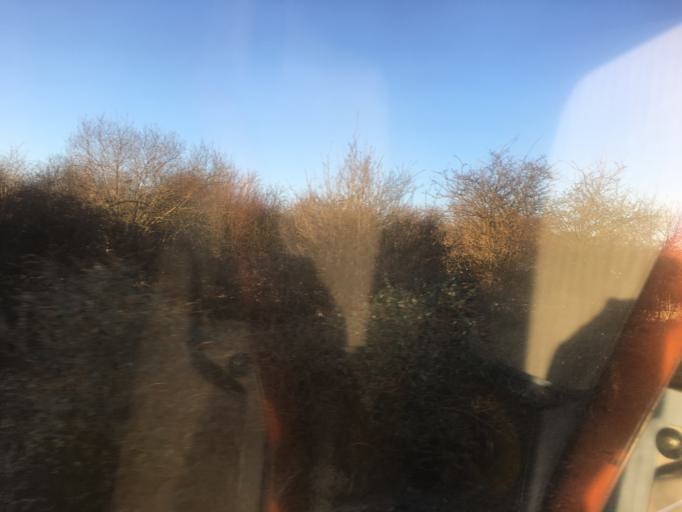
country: GB
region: England
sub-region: Derbyshire
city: Long Eaton
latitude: 52.8938
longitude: -1.2521
